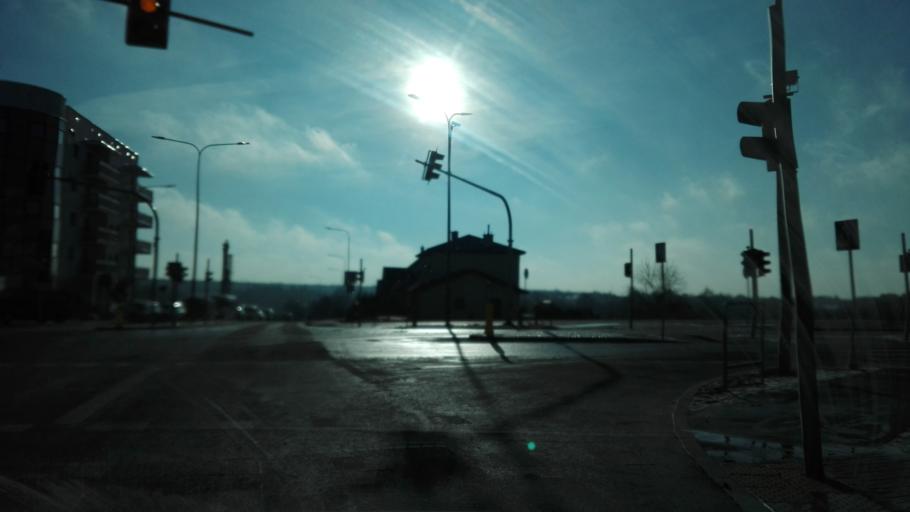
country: PL
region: Lublin Voivodeship
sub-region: Powiat lubelski
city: Kozubszczyzna
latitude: 51.2235
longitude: 22.4926
